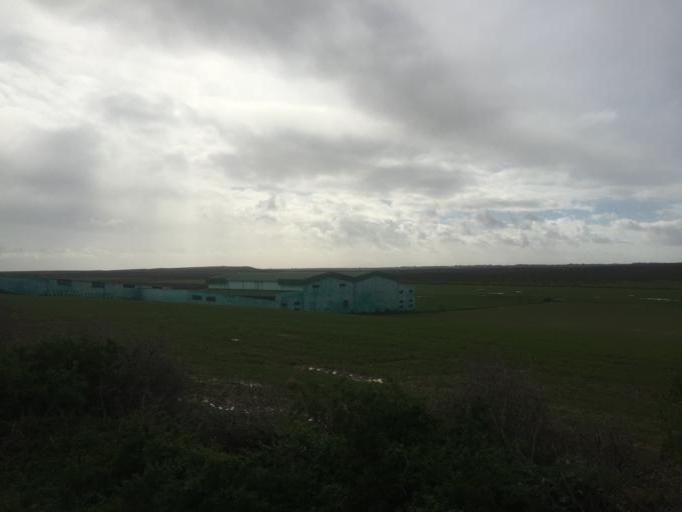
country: TN
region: Nabul
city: Menzel Heurr
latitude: 36.8345
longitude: 10.9600
